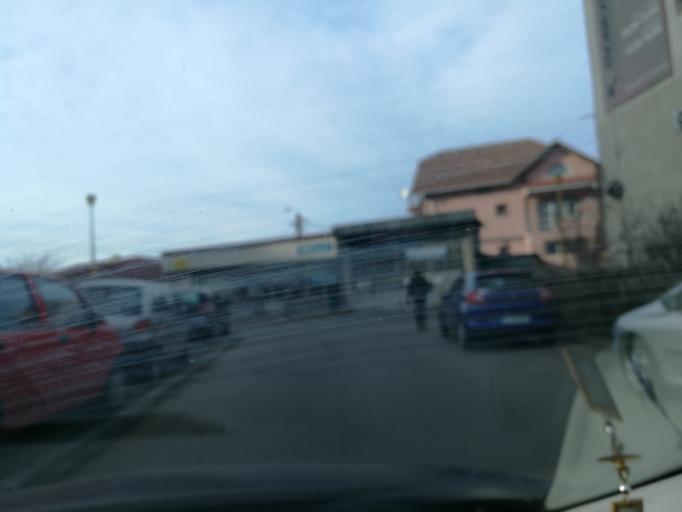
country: RO
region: Constanta
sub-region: Municipiul Constanta
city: Constanta
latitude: 44.1739
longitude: 28.6108
